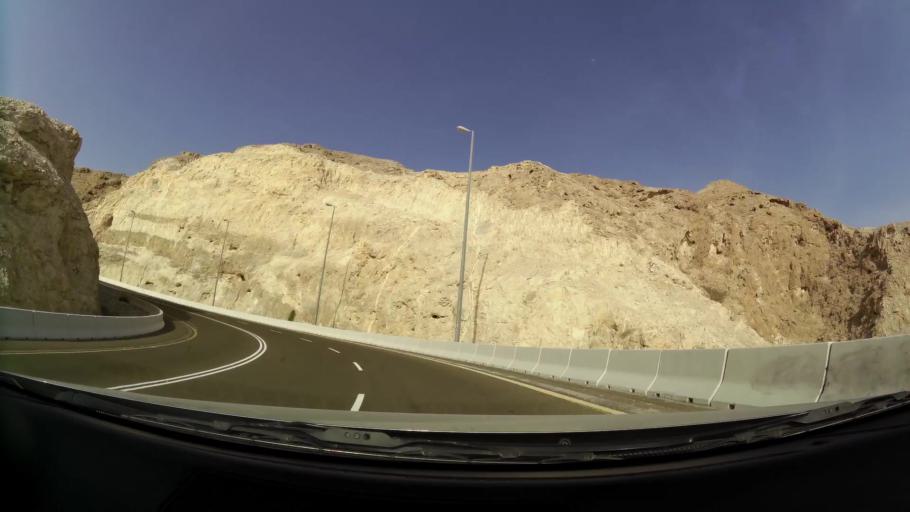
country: AE
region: Abu Dhabi
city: Al Ain
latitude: 24.0931
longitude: 55.7575
